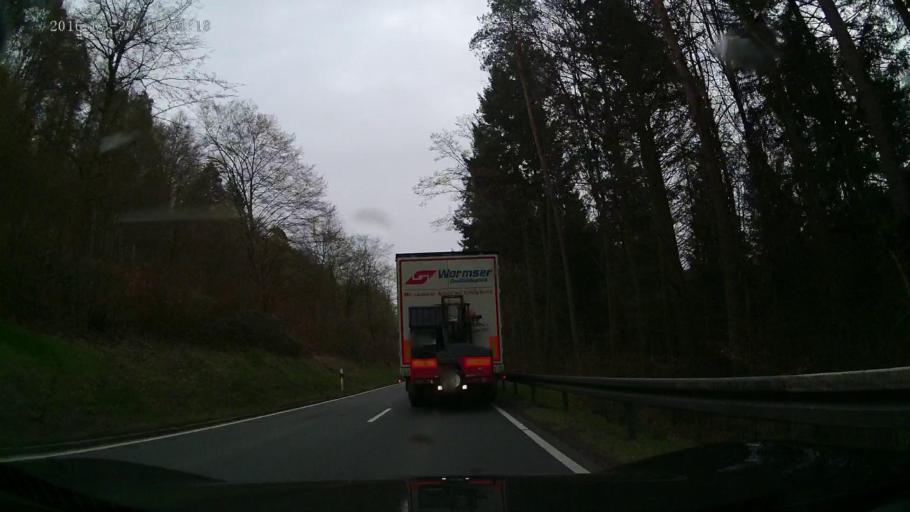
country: DE
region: Baden-Wuerttemberg
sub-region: Karlsruhe Region
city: Walldurn
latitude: 49.6173
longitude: 9.3158
